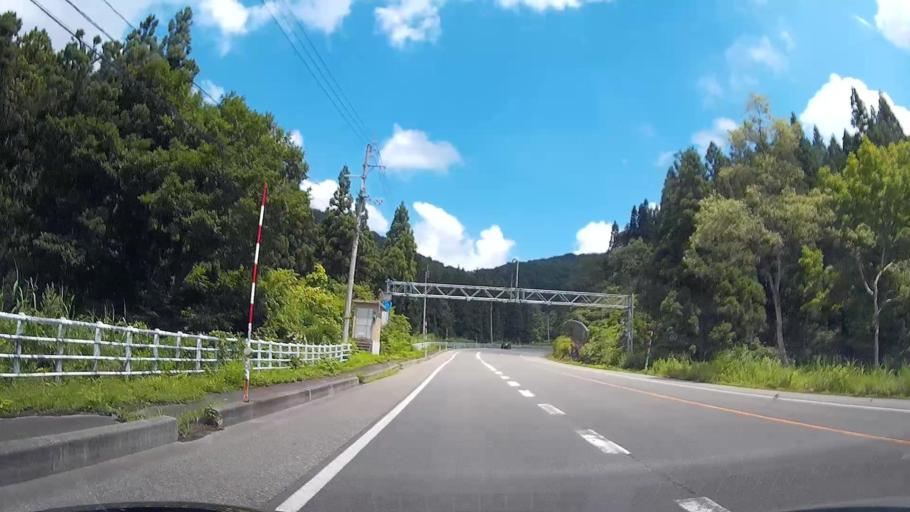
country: JP
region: Niigata
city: Shiozawa
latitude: 36.9052
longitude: 138.7847
